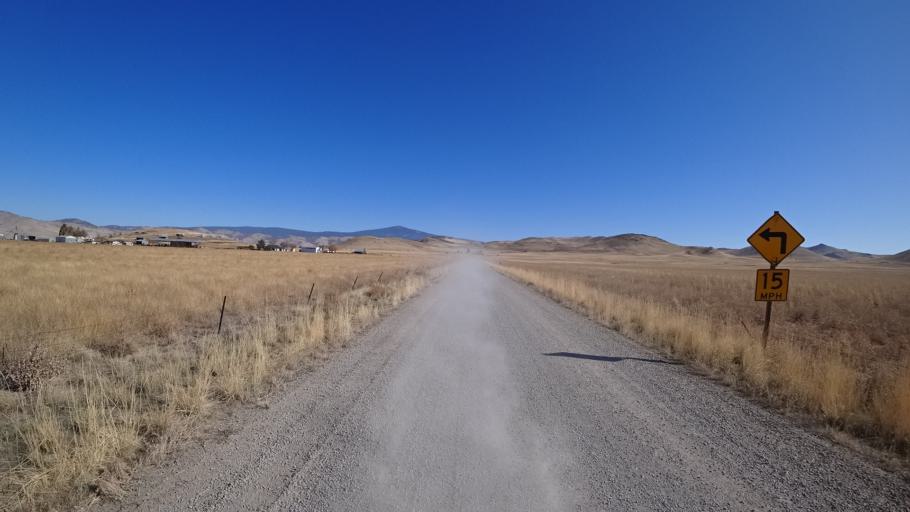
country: US
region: California
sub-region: Siskiyou County
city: Montague
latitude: 41.7865
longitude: -122.4376
